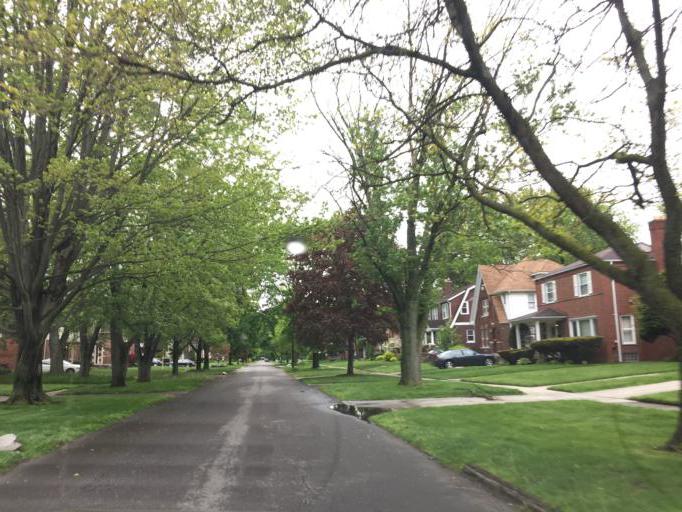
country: US
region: Michigan
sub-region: Oakland County
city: Southfield
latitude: 42.4149
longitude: -83.2305
